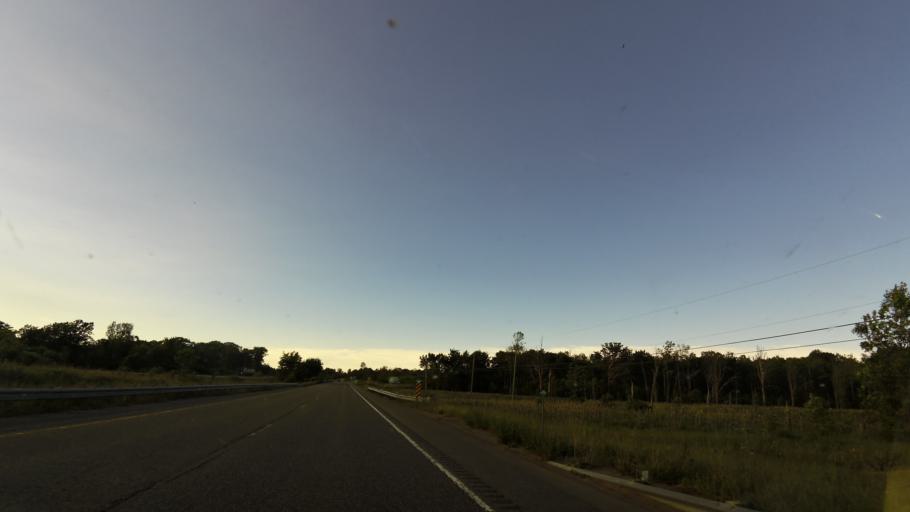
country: CA
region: Ontario
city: Midland
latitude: 44.8237
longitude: -79.7375
